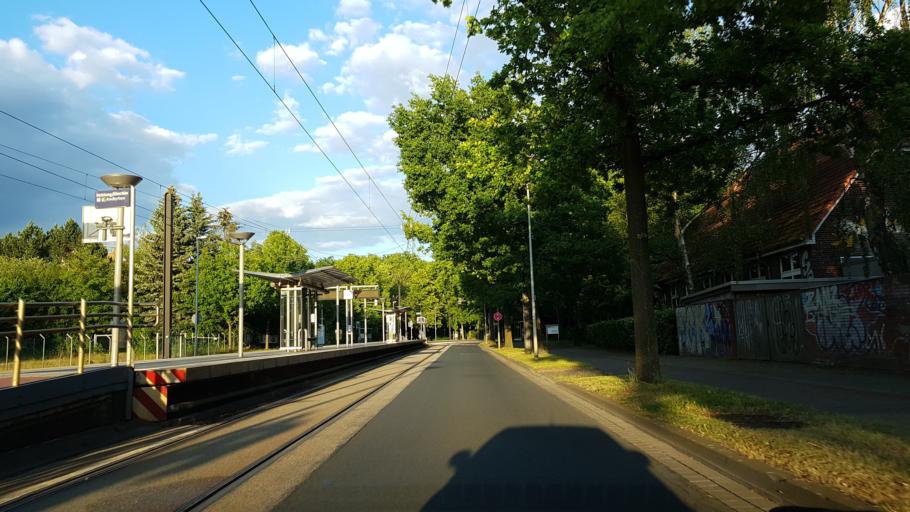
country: DE
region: Lower Saxony
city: Laatzen
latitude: 52.3697
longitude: 9.8073
